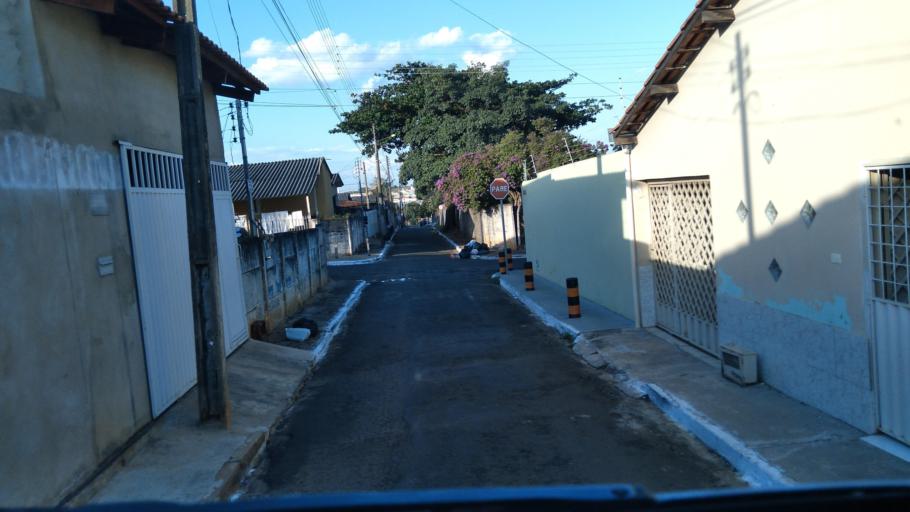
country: BR
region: Goias
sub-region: Mineiros
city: Mineiros
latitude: -17.5616
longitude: -52.5476
